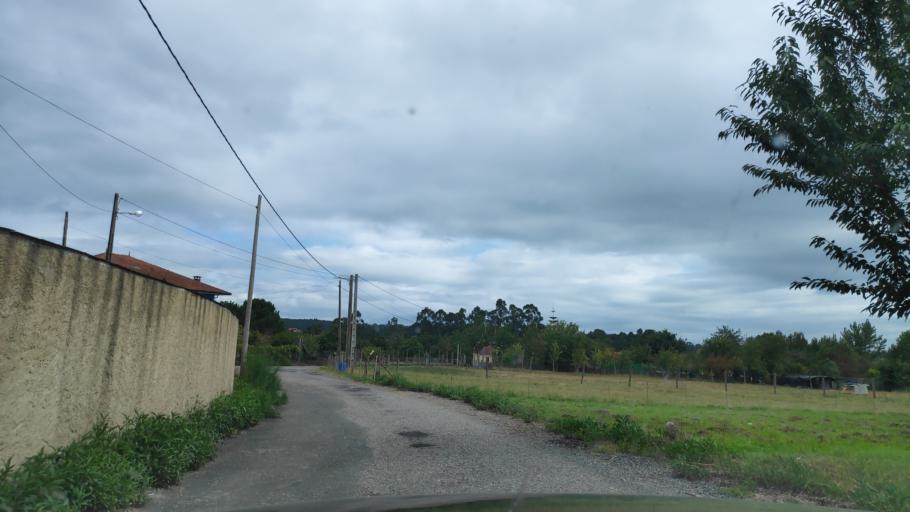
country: ES
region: Galicia
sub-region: Provincia da Coruna
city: Rianxo
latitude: 42.6743
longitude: -8.8141
